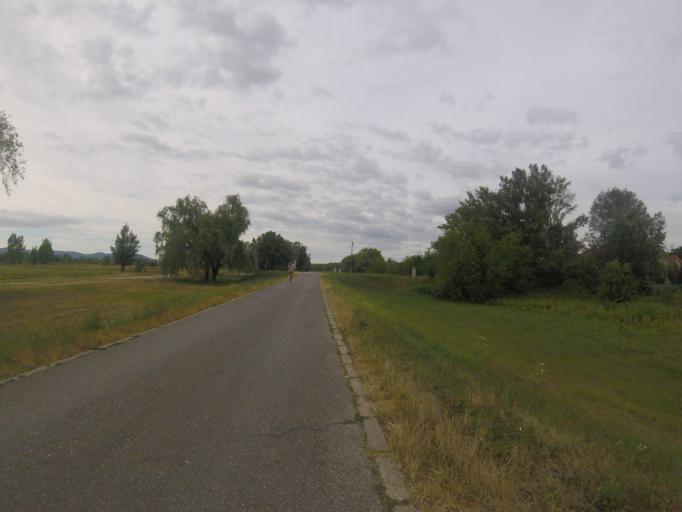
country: HU
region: Pest
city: Budakalasz
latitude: 47.6174
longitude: 19.0792
